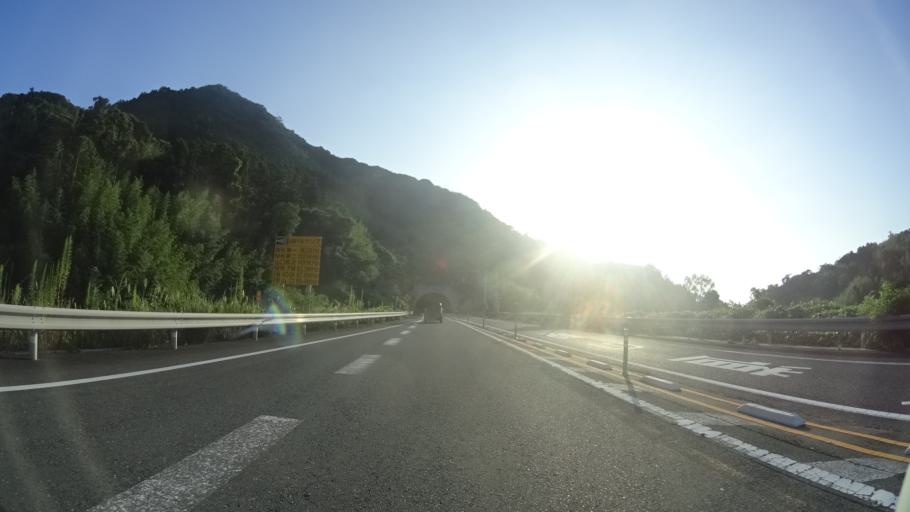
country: JP
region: Yamaguchi
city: Hagi
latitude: 34.3873
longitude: 131.3204
